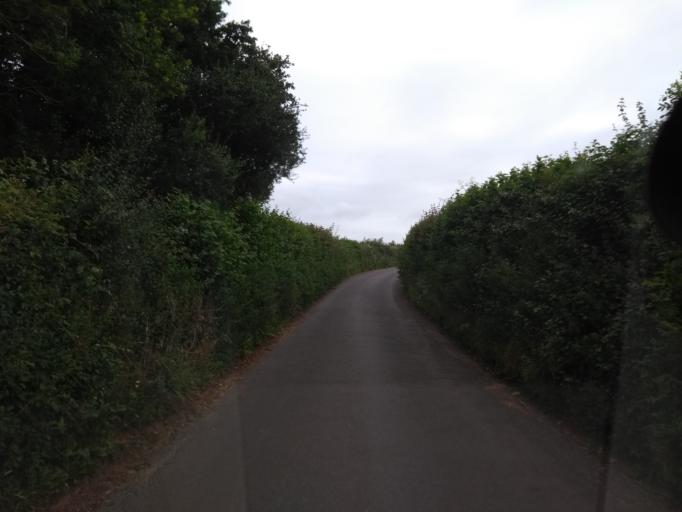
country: GB
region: England
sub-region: Somerset
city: Wiveliscombe
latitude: 51.0315
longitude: -3.2479
